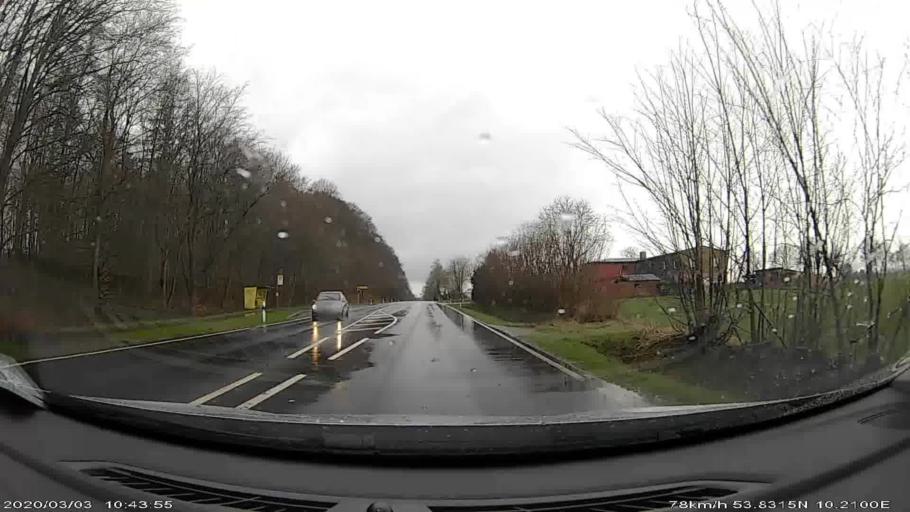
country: DE
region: Schleswig-Holstein
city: Seth
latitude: 53.8318
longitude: 10.2073
